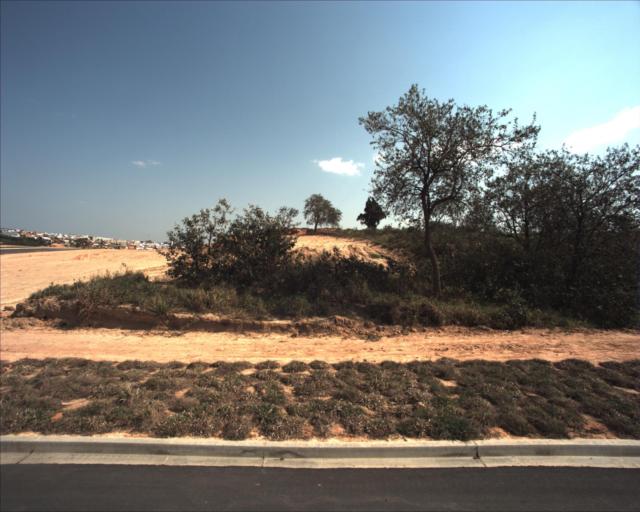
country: BR
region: Sao Paulo
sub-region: Sorocaba
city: Sorocaba
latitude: -23.4399
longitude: -47.4882
